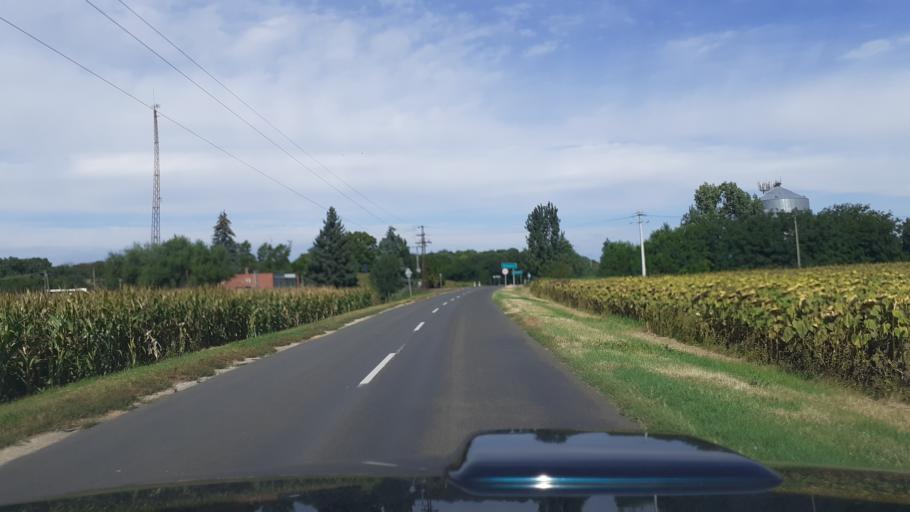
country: HU
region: Fejer
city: Gardony
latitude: 47.1301
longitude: 18.6766
